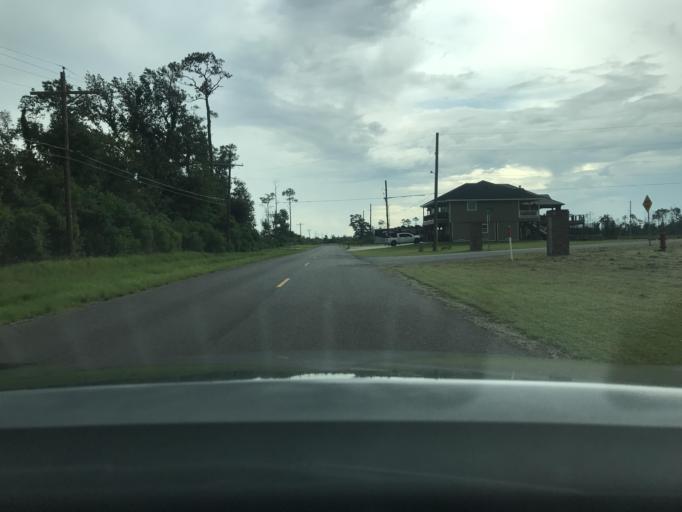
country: US
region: Louisiana
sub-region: Calcasieu Parish
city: Westlake
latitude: 30.2570
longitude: -93.2259
